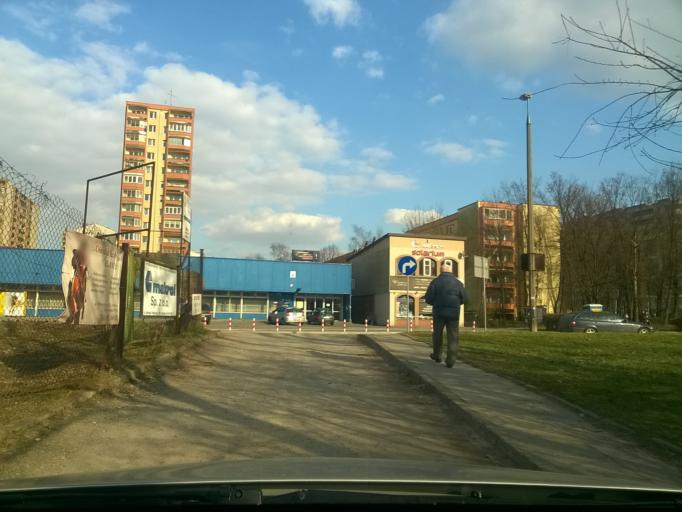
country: PL
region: Lesser Poland Voivodeship
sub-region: Krakow
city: Krakow
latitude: 50.0900
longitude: 19.9733
